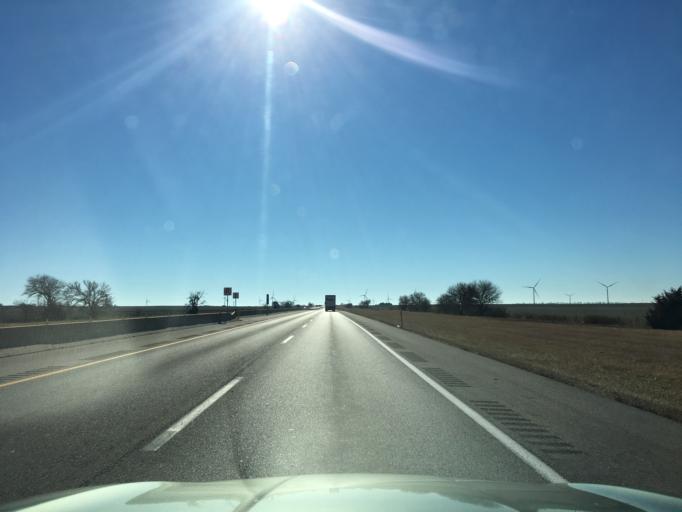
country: US
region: Kansas
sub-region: Sumner County
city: Wellington
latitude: 37.1792
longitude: -97.3396
